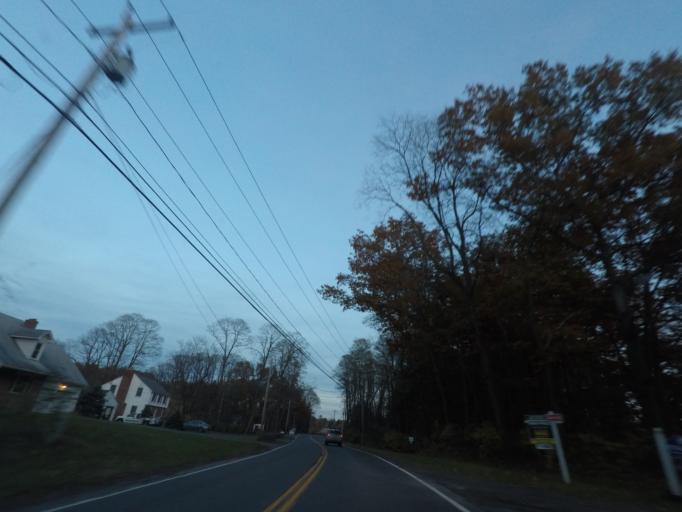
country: US
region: New York
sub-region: Schenectady County
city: Rotterdam
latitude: 42.7482
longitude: -73.9125
